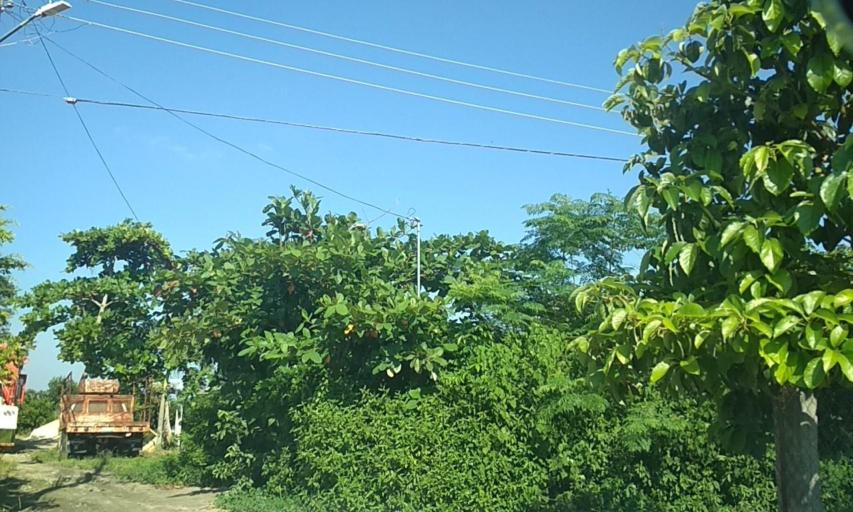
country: MX
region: Veracruz
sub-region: Martinez de la Torre
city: La Union Paso Largo
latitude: 20.1448
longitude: -96.9975
